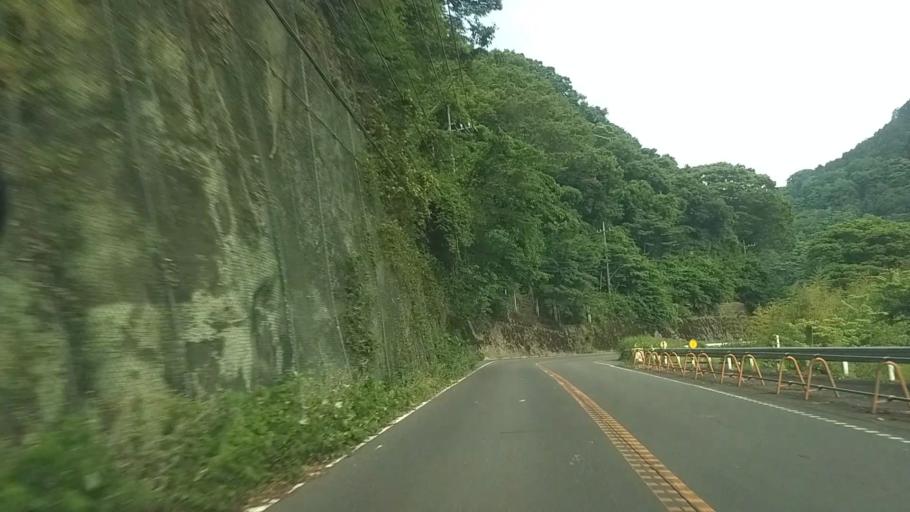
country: JP
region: Shizuoka
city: Gotemba
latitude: 35.3603
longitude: 139.0596
